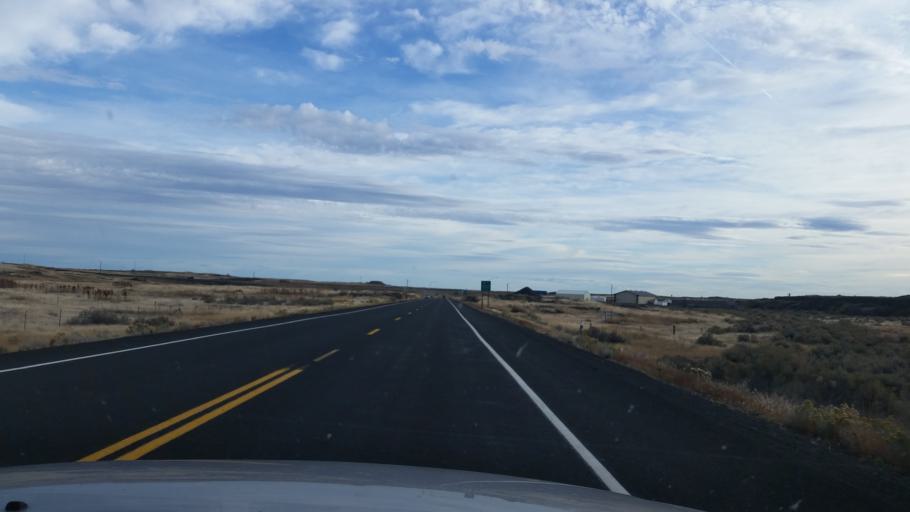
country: US
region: Washington
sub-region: Lincoln County
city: Davenport
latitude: 47.3145
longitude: -117.9737
